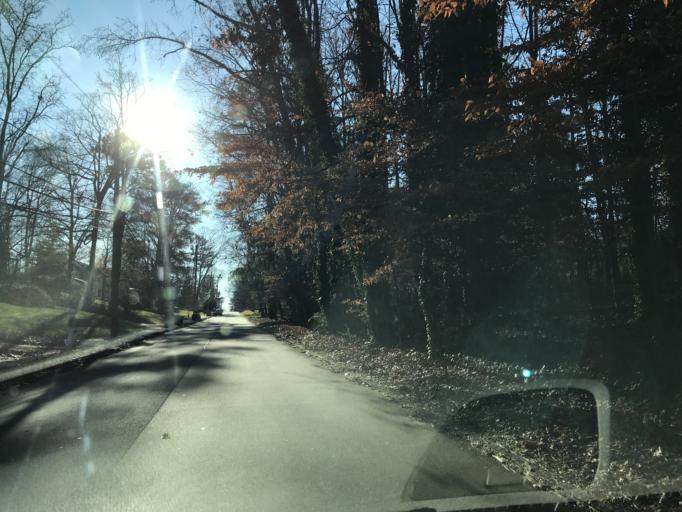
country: US
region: Georgia
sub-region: DeKalb County
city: North Atlanta
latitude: 33.8827
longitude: -84.3374
